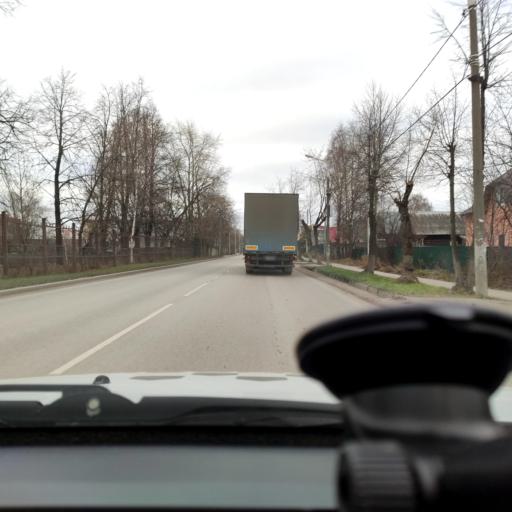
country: RU
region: Perm
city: Perm
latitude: 58.1105
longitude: 56.2967
